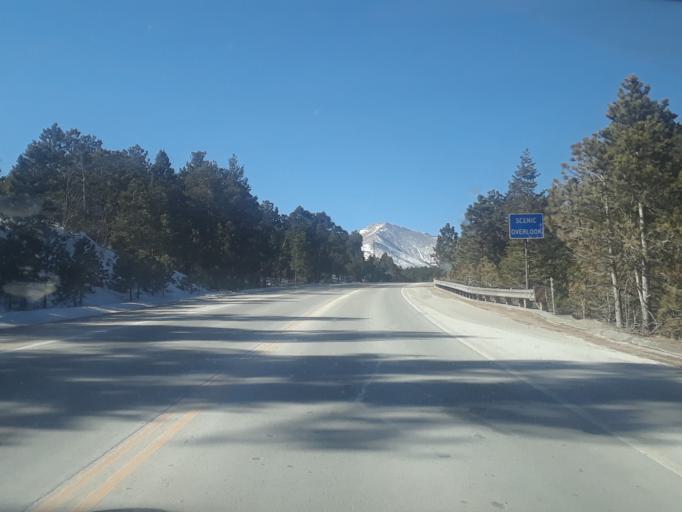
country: US
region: Colorado
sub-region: Larimer County
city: Estes Park
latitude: 40.1843
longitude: -105.4808
